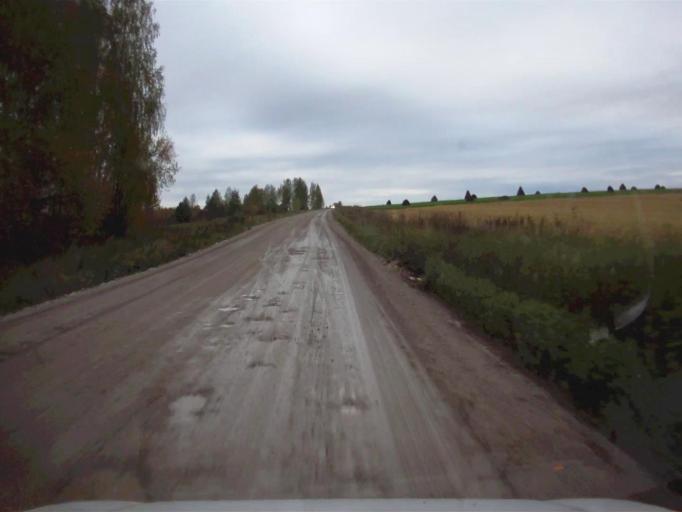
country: RU
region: Sverdlovsk
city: Mikhaylovsk
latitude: 56.1765
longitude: 59.2117
